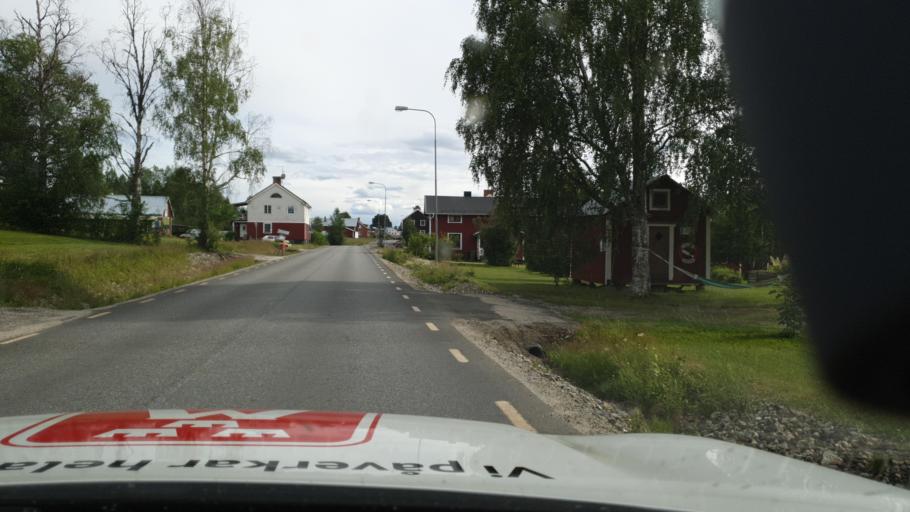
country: SE
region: Vaesterbotten
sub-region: Norsjo Kommun
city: Norsjoe
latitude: 64.5328
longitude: 19.3466
